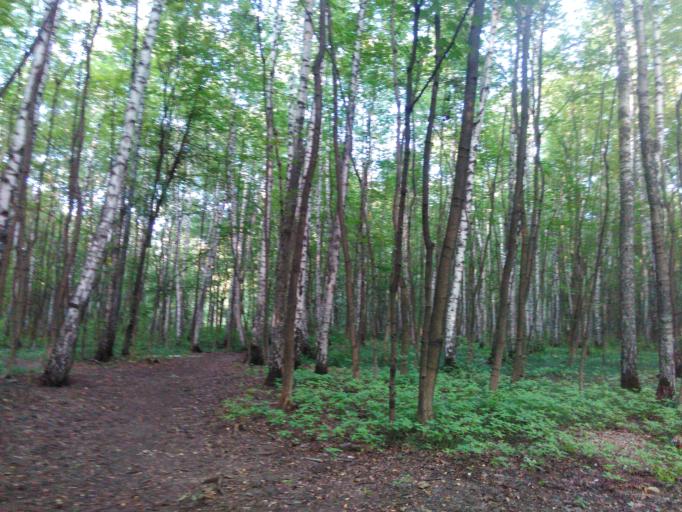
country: RU
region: Moscow
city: Sokol'niki
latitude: 55.8091
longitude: 37.6669
